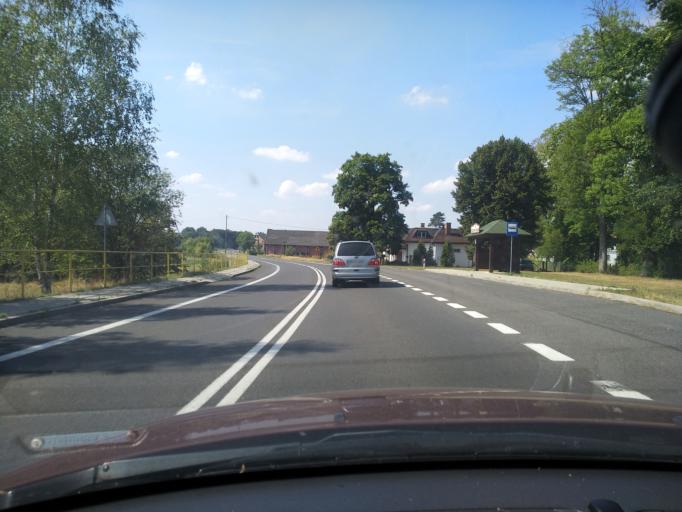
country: PL
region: Lower Silesian Voivodeship
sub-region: Powiat lubanski
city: Olszyna
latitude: 51.0823
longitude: 15.3325
